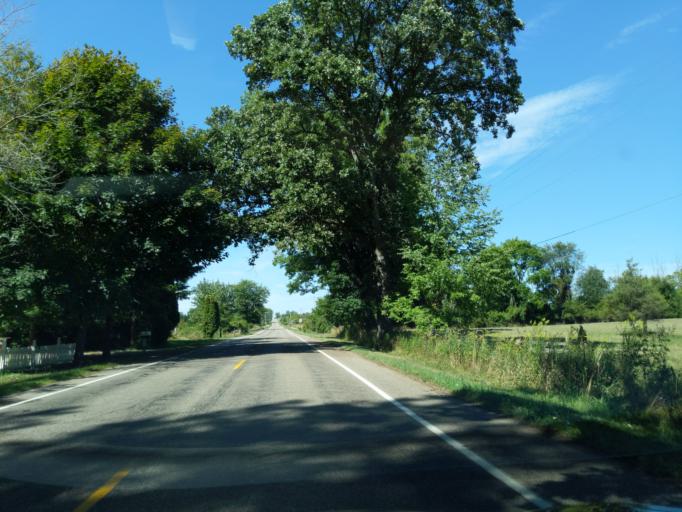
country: US
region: Michigan
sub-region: Eaton County
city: Potterville
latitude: 42.6259
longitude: -84.7721
